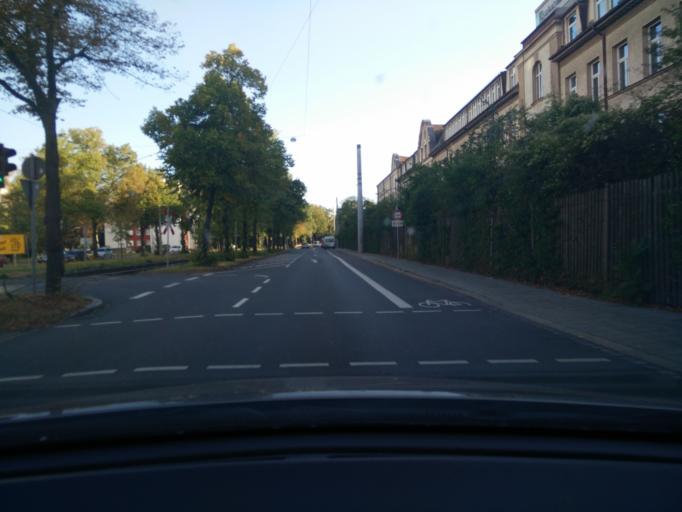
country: DE
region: Bavaria
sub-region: Regierungsbezirk Mittelfranken
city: Nuernberg
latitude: 49.4227
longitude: 11.0849
